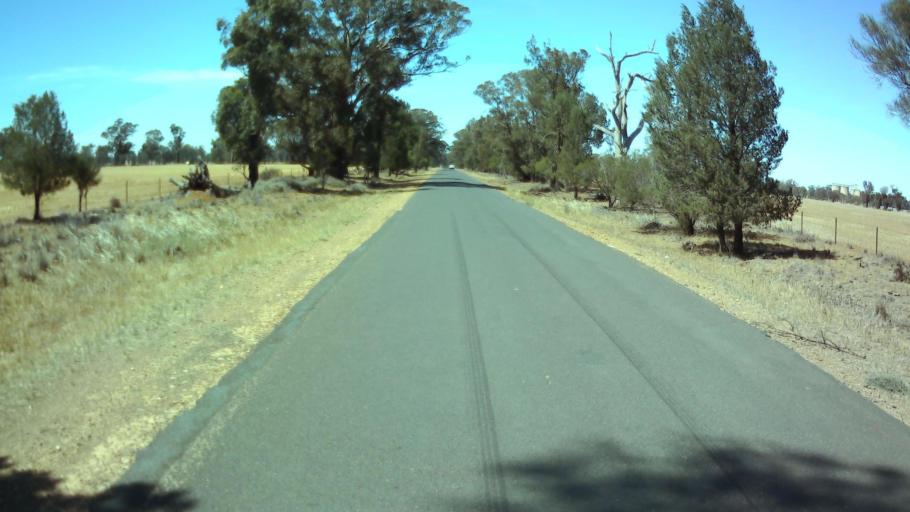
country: AU
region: New South Wales
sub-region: Weddin
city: Grenfell
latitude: -34.1103
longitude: 147.8858
